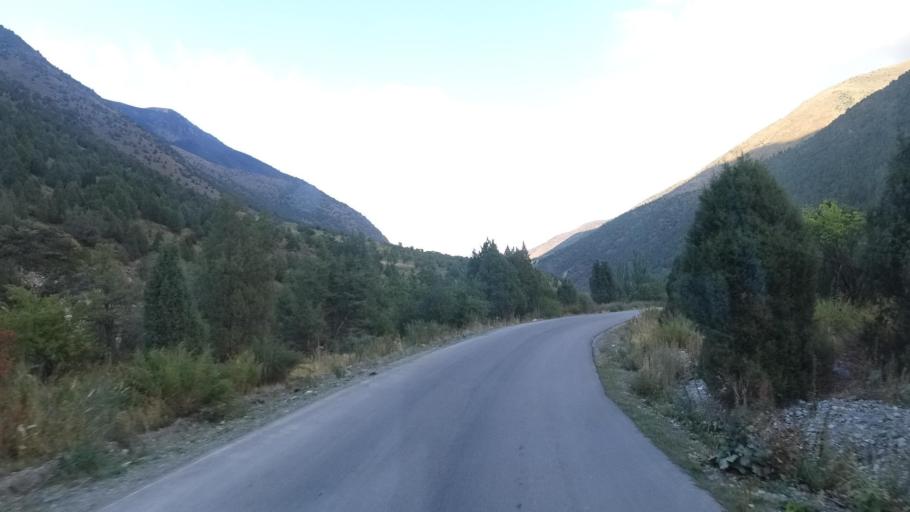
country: KG
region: Chuy
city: Bishkek
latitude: 42.6033
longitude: 74.4804
